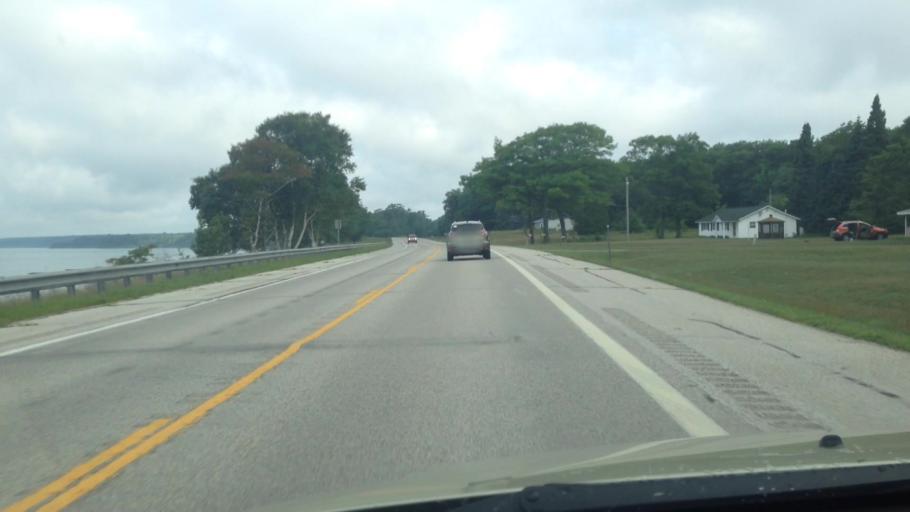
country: US
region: Michigan
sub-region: Mackinac County
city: Saint Ignace
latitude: 46.0006
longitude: -84.9942
